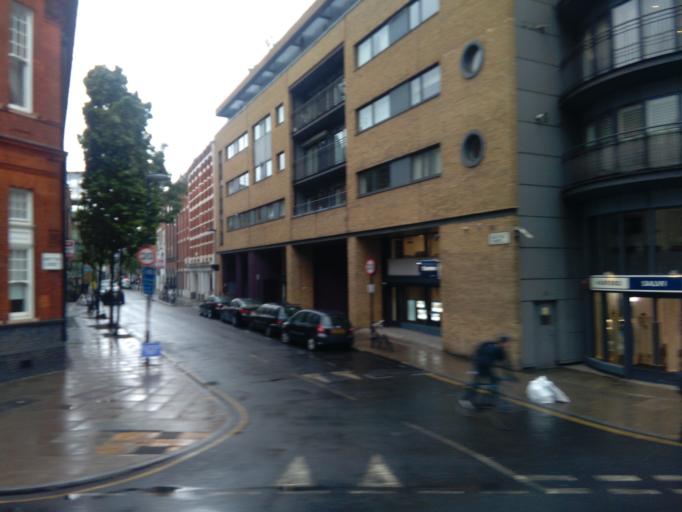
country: GB
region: England
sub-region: Greater London
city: Clerkenwell
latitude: 51.5216
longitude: -0.1052
